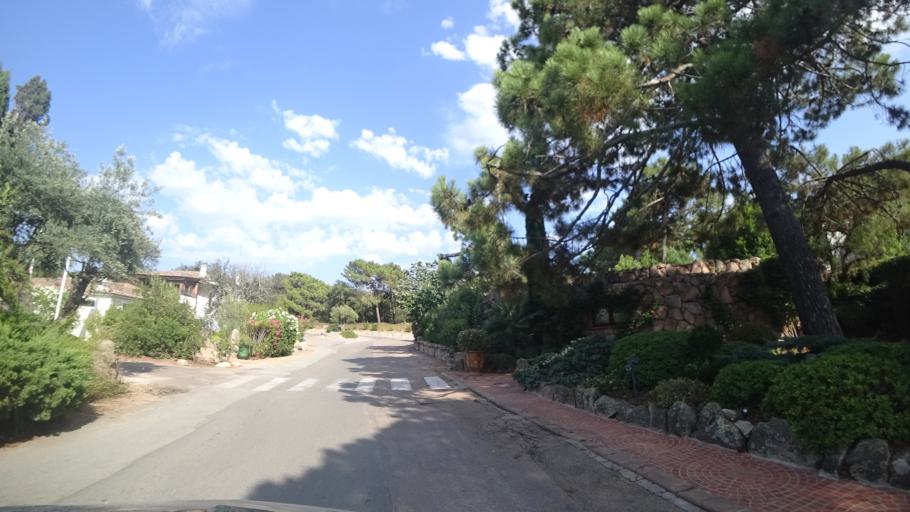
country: FR
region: Corsica
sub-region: Departement de la Corse-du-Sud
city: Porto-Vecchio
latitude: 41.6221
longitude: 9.3387
